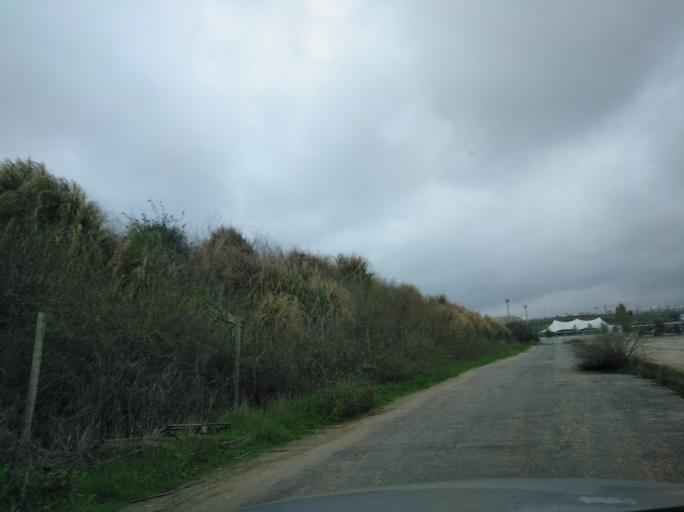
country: PT
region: Lisbon
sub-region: Loures
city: Bobadela
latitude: 38.7943
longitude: -9.0924
